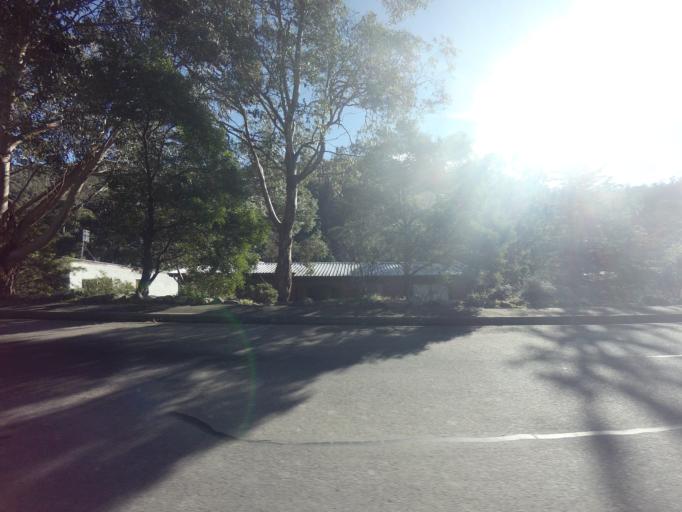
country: AU
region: Tasmania
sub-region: Glenorchy
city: Berriedale
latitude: -42.8176
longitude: 147.2236
